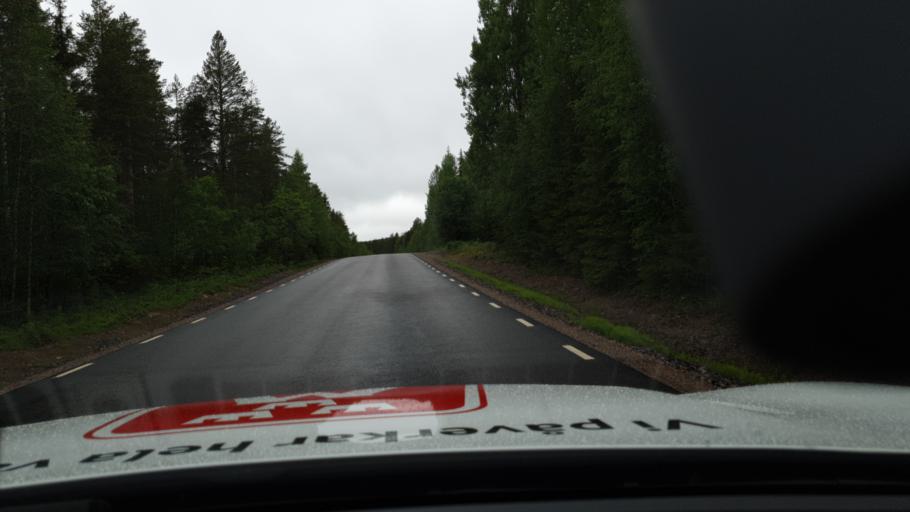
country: SE
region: Norrbotten
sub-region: Overtornea Kommun
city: OEvertornea
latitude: 66.4289
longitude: 23.5270
